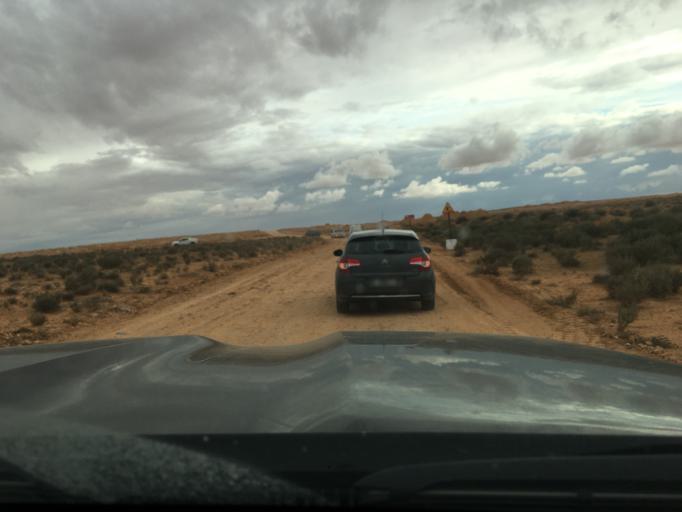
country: TN
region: Madanin
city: Medenine
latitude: 33.2604
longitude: 10.5732
